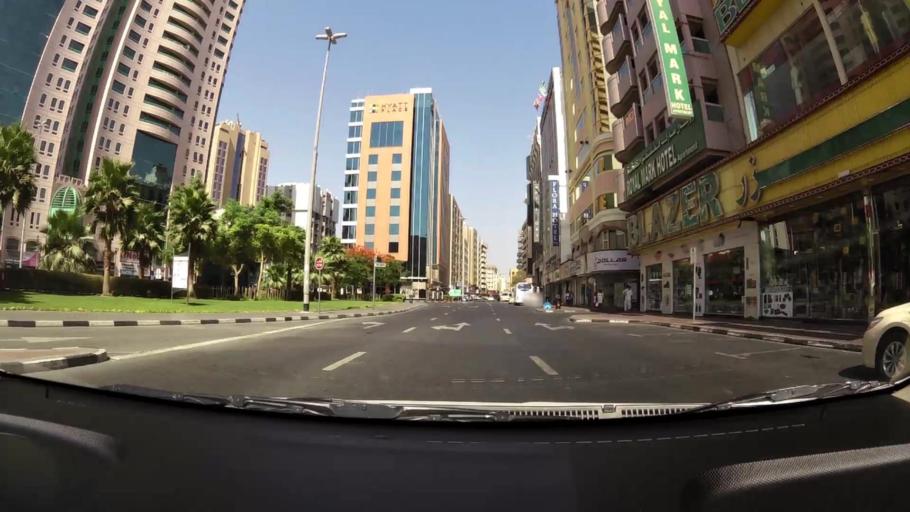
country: AE
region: Ash Shariqah
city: Sharjah
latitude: 25.2690
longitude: 55.3065
